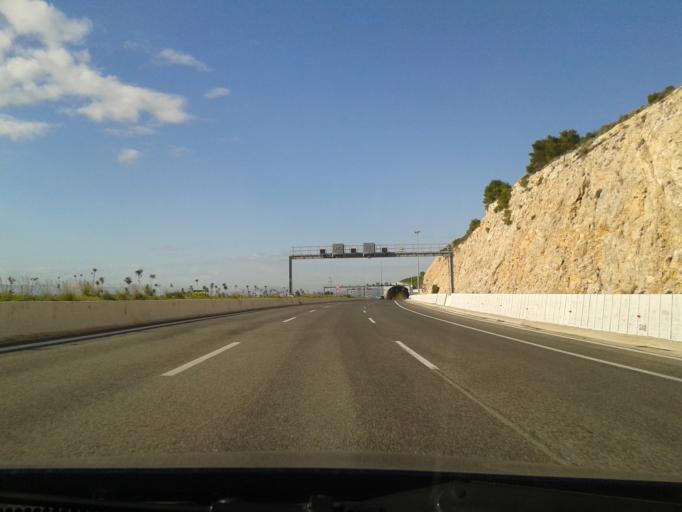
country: GR
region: Attica
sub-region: Nomarchia Dytikis Attikis
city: Megara
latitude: 37.9737
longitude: 23.3073
